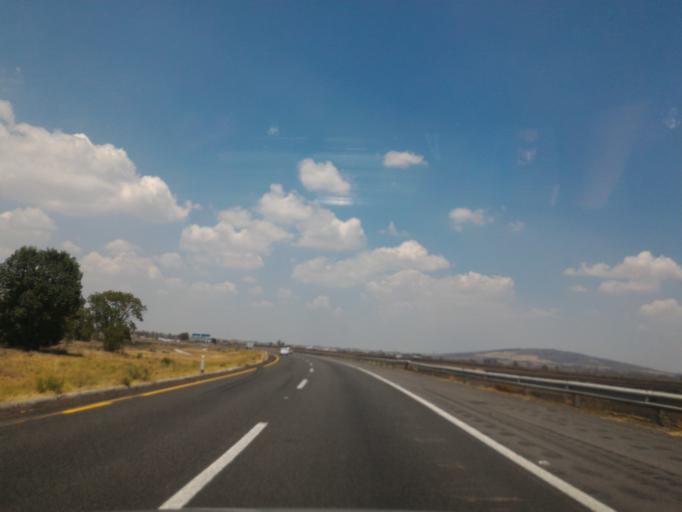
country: MX
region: Jalisco
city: Tepatitlan de Morelos
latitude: 20.8992
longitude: -102.6990
